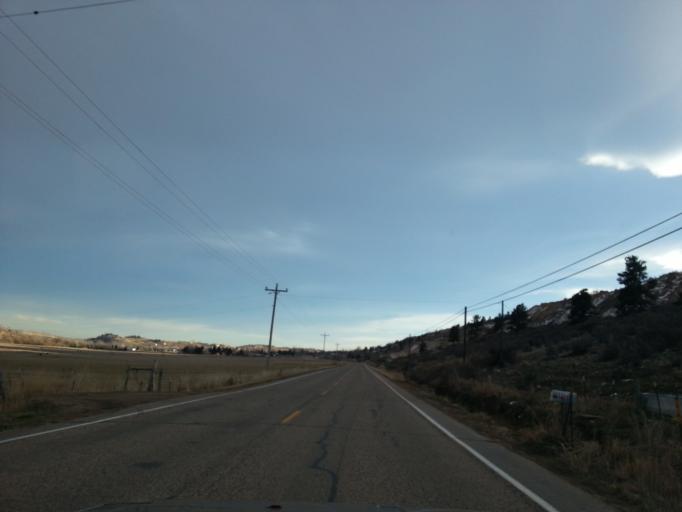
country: US
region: Colorado
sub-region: Larimer County
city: Loveland
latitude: 40.4481
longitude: -105.2034
